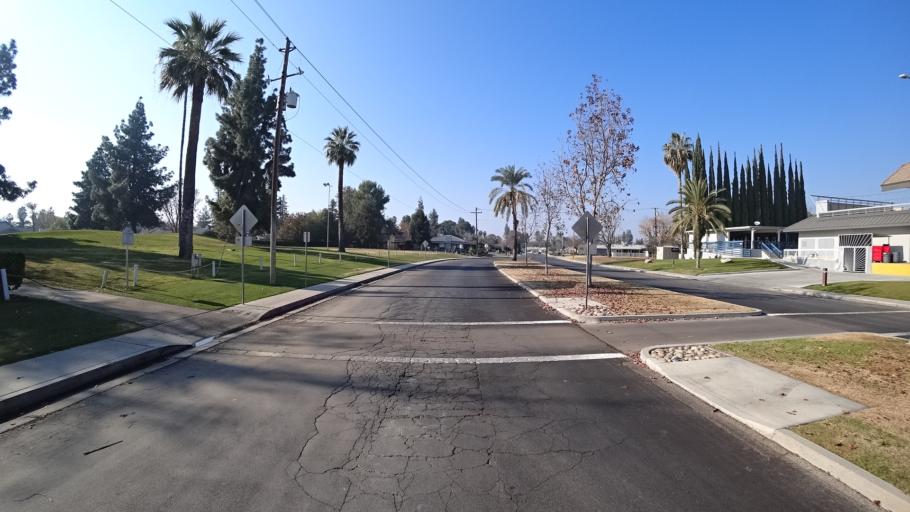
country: US
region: California
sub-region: Kern County
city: Greenacres
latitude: 35.3438
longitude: -119.0702
